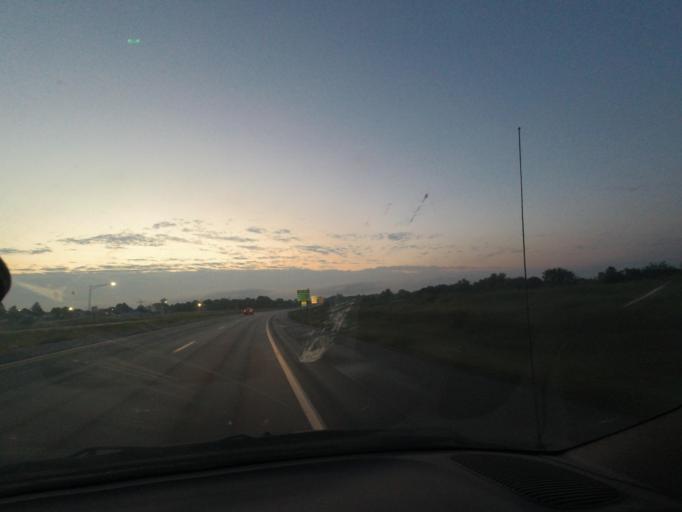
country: US
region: Missouri
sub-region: Linn County
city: Brookfield
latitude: 39.7797
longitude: -93.1051
